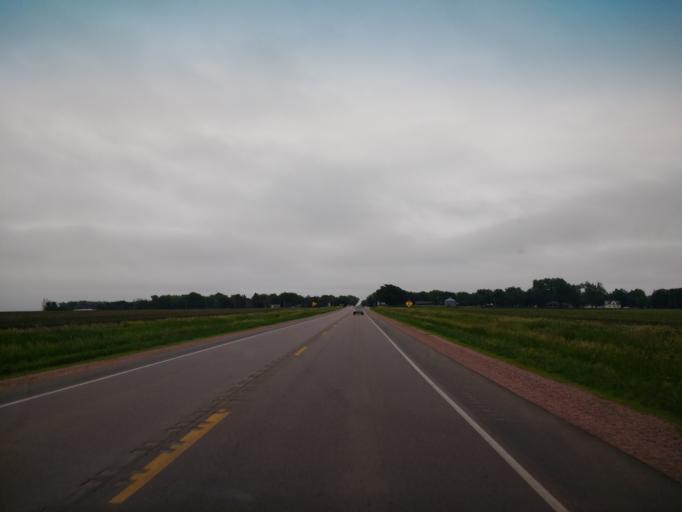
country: US
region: Iowa
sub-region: O'Brien County
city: Sanborn
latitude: 43.1861
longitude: -95.6699
